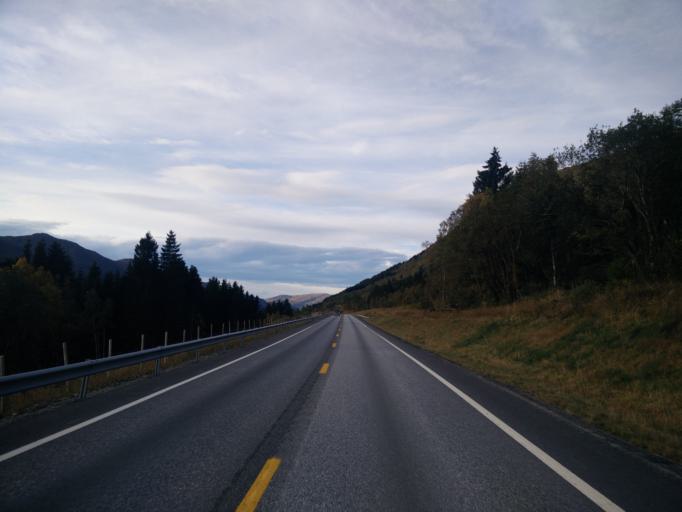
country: NO
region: More og Romsdal
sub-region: Gjemnes
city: Batnfjordsora
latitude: 62.9451
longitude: 7.7467
